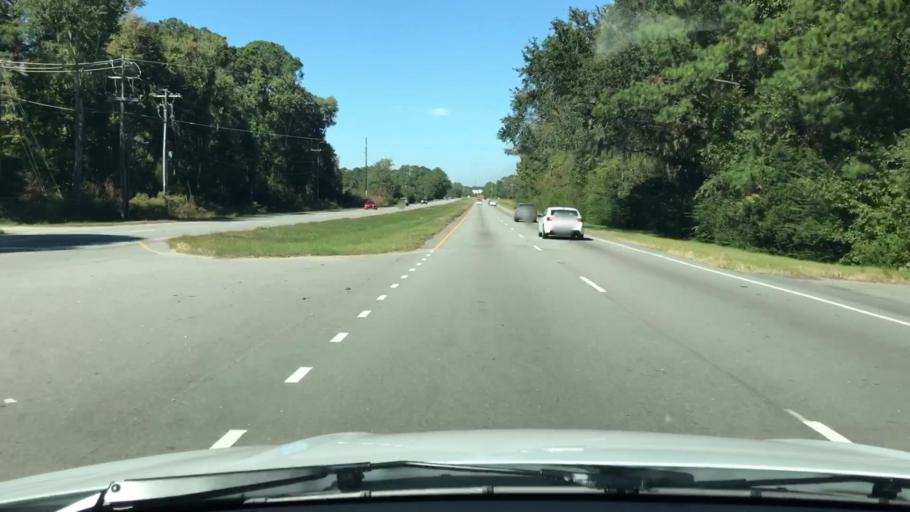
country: US
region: South Carolina
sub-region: Beaufort County
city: Laurel Bay
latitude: 32.4984
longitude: -80.7433
